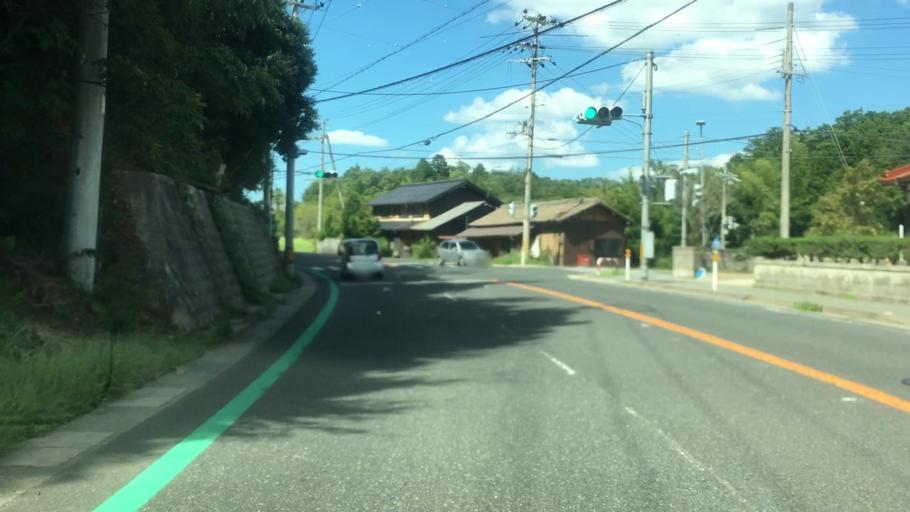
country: JP
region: Kyoto
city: Miyazu
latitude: 35.6125
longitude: 135.0542
